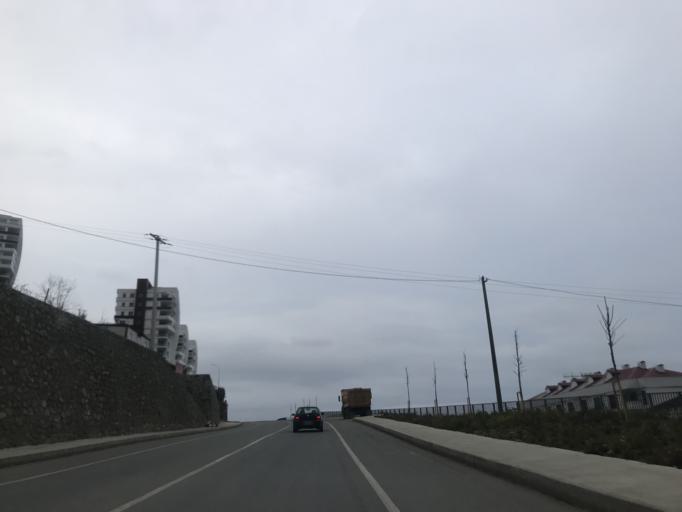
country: TR
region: Trabzon
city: Akcaabat
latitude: 41.0010
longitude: 39.6268
